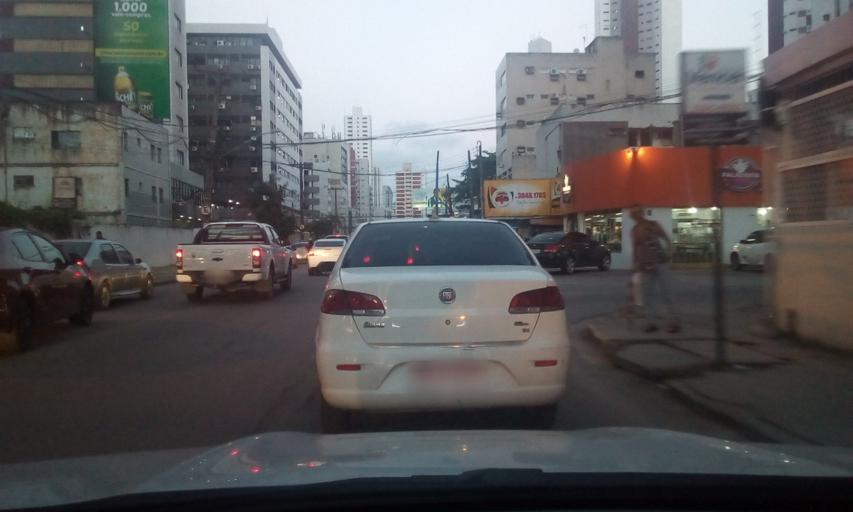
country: BR
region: Pernambuco
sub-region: Recife
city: Recife
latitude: -8.1243
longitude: -34.9073
